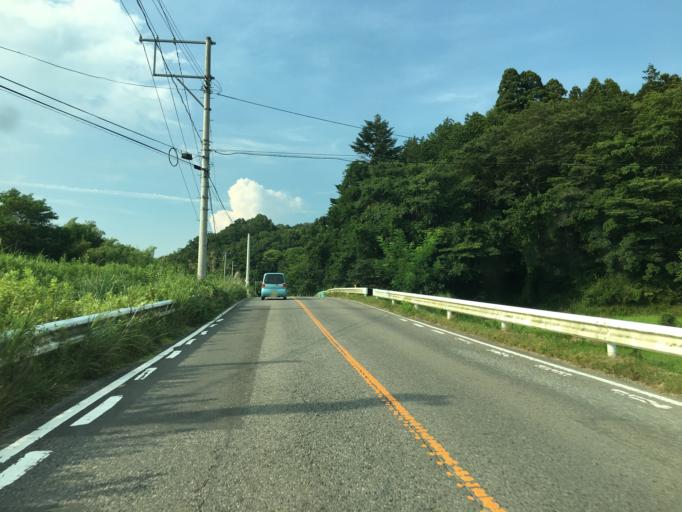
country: JP
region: Fukushima
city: Motomiya
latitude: 37.4637
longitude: 140.4251
